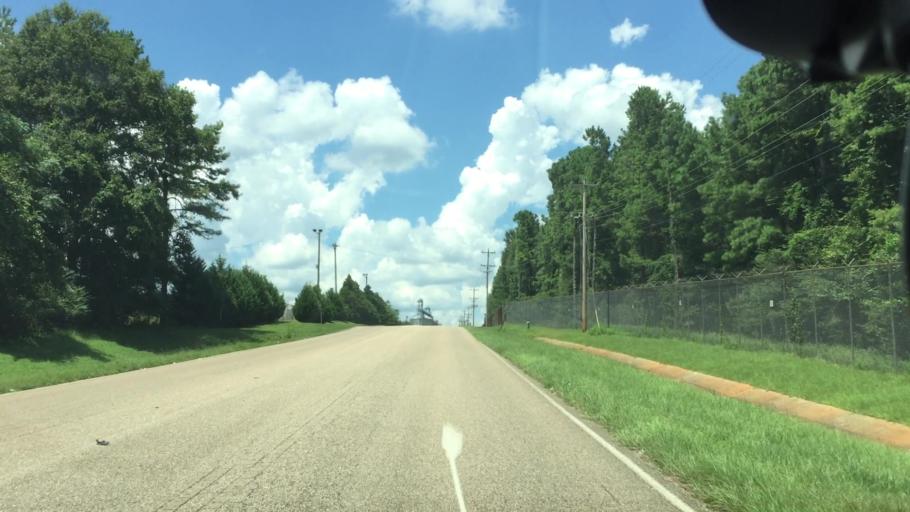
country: US
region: Alabama
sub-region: Pike County
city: Troy
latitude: 31.7780
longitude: -85.9787
